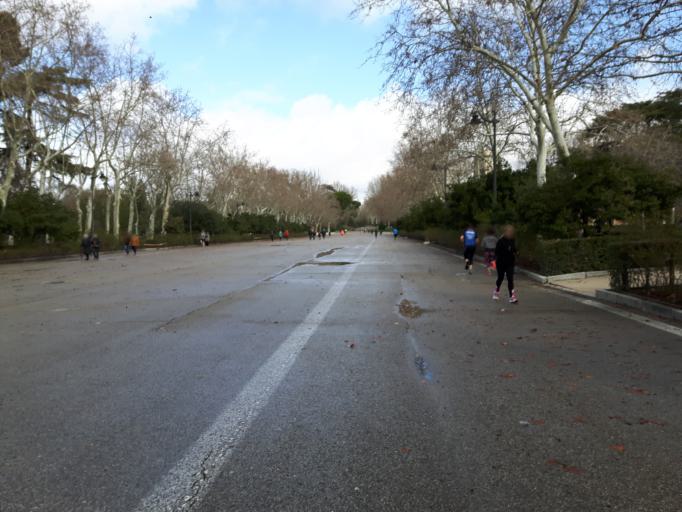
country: ES
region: Madrid
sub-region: Provincia de Madrid
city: Retiro
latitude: 40.4145
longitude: -3.6796
